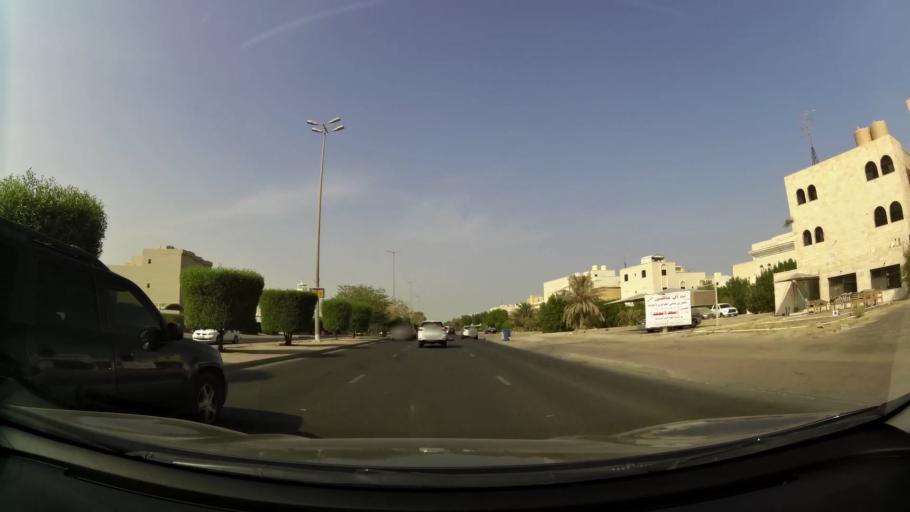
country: KW
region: Al Ahmadi
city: Ar Riqqah
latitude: 29.1618
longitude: 48.0855
